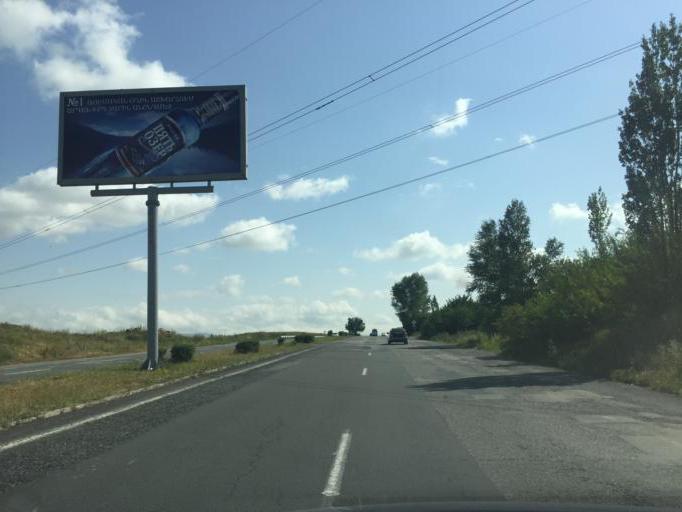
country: AM
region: Kotayk'i Marz
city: Hrazdan
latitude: 40.4975
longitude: 44.7853
